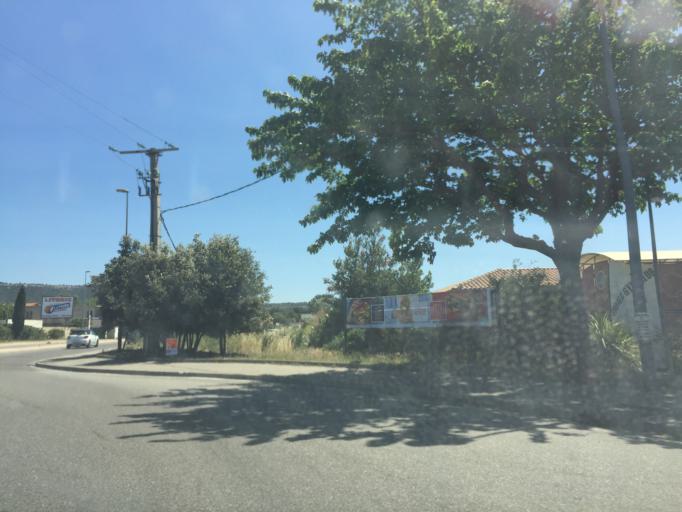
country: FR
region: Provence-Alpes-Cote d'Azur
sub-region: Departement des Bouches-du-Rhone
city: Rognac
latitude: 43.4852
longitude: 5.2227
